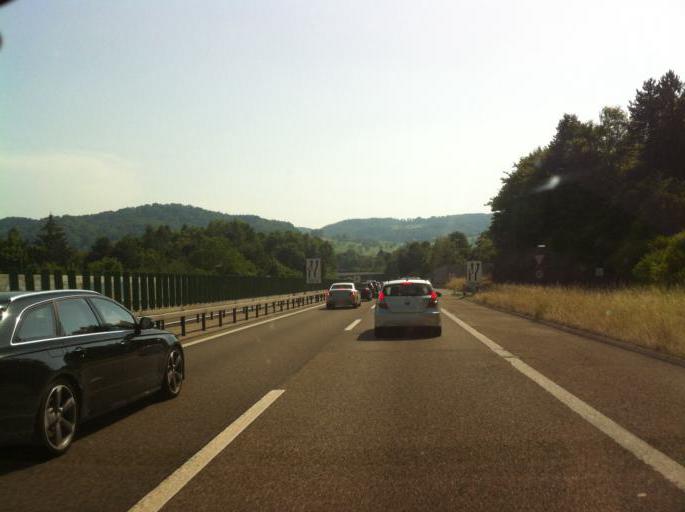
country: CH
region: Zurich
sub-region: Bezirk Winterthur
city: Wuelflingen (Kreis 6) / Lindenplatz
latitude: 47.5157
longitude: 8.6929
